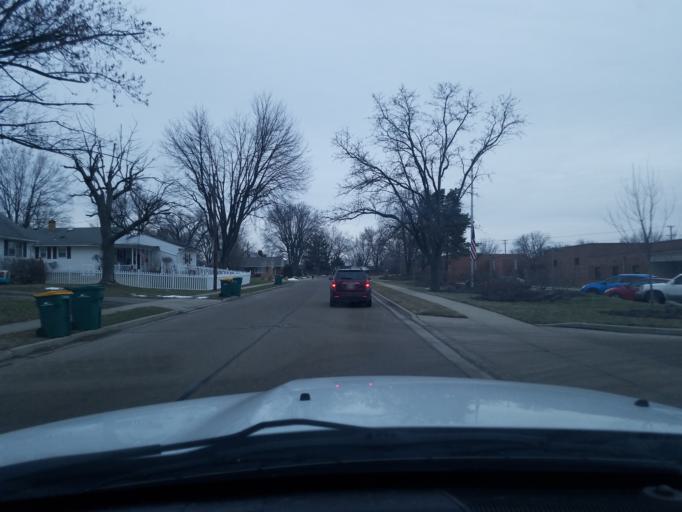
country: US
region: Ohio
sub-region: Montgomery County
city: Kettering
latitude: 39.7057
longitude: -84.1501
